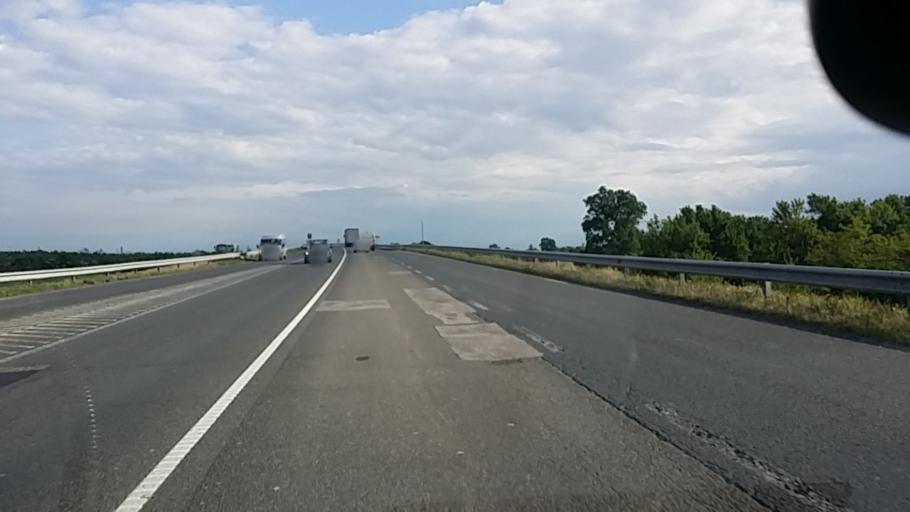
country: HU
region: Gyor-Moson-Sopron
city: Rajka
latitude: 47.9394
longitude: 17.1667
